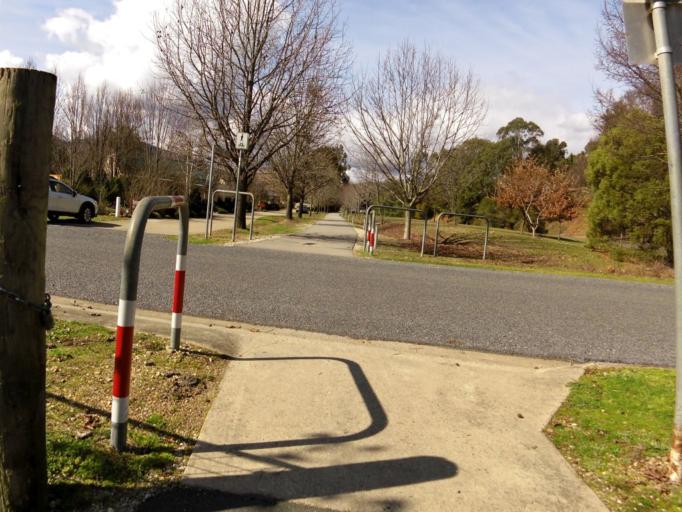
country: AU
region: Victoria
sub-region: Alpine
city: Mount Beauty
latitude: -36.7301
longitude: 146.9530
